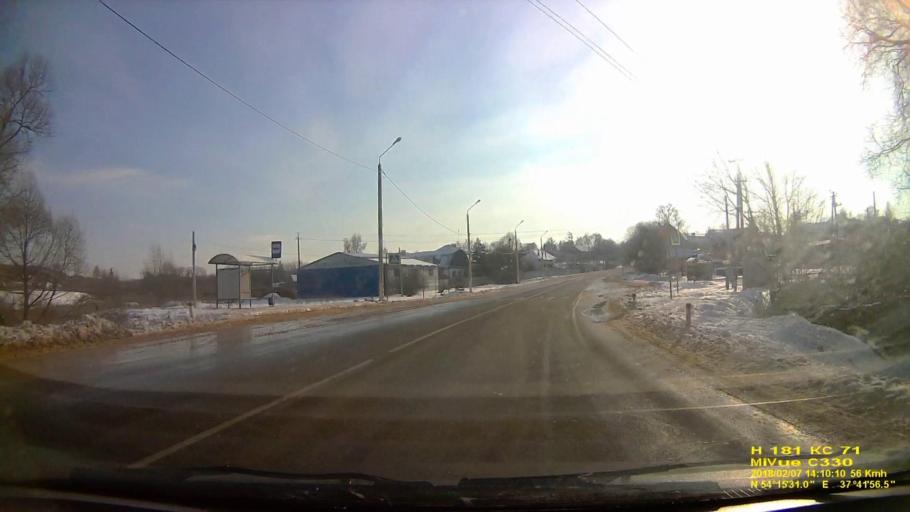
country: RU
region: Tula
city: Gorelki
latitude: 54.2585
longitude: 37.6990
